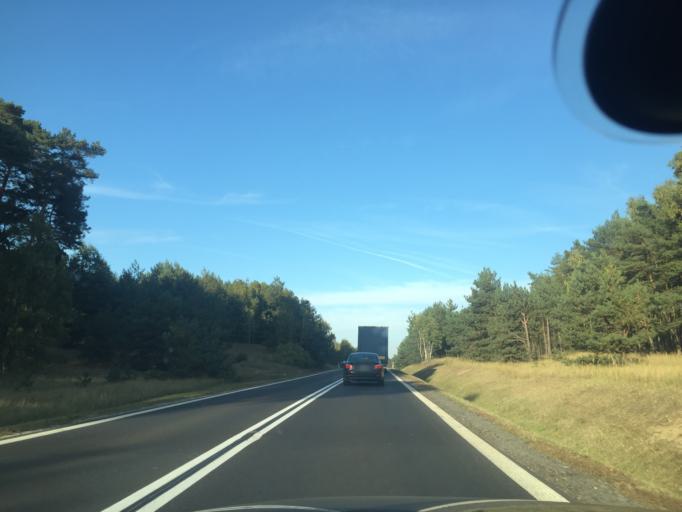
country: PL
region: Kujawsko-Pomorskie
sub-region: Powiat torunski
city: Wielka Nieszawka
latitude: 52.9431
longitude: 18.5193
